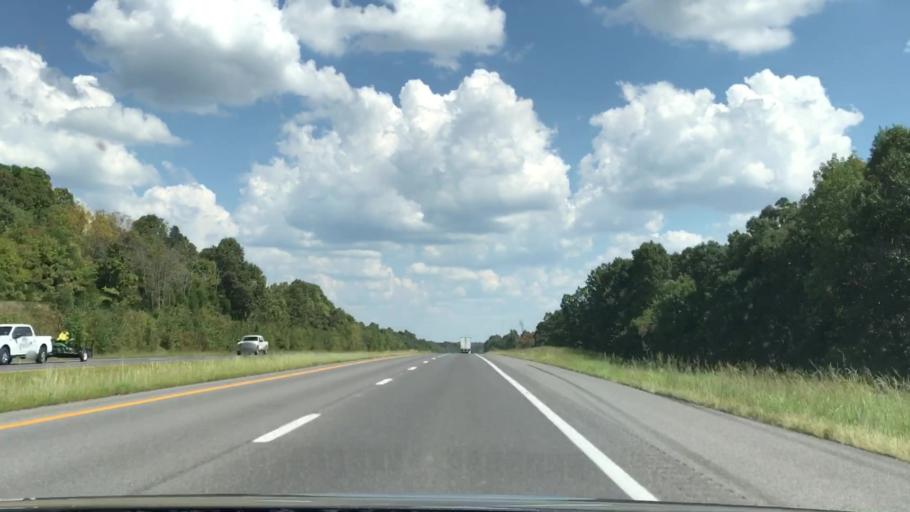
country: US
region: Kentucky
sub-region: Lyon County
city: Eddyville
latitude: 37.1074
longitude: -87.9818
